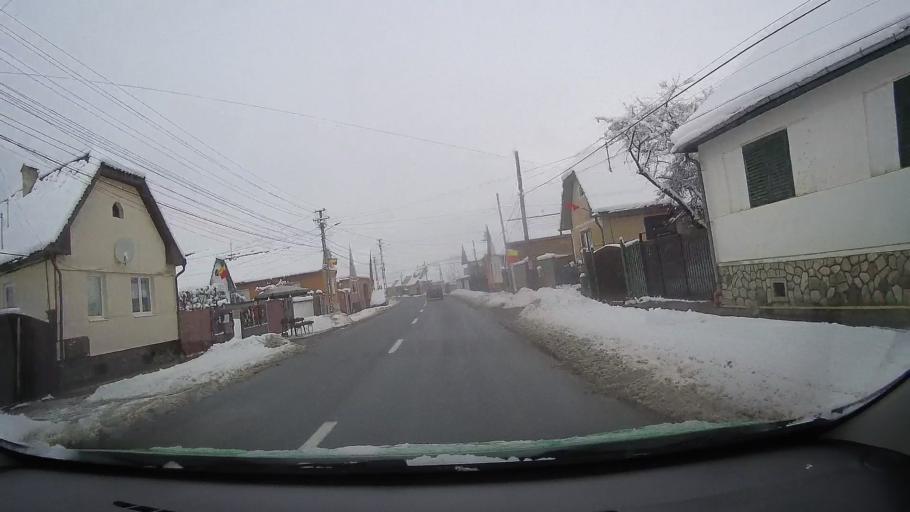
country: RO
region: Sibiu
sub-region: Comuna Cristian
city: Cristian
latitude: 45.7774
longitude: 24.0276
